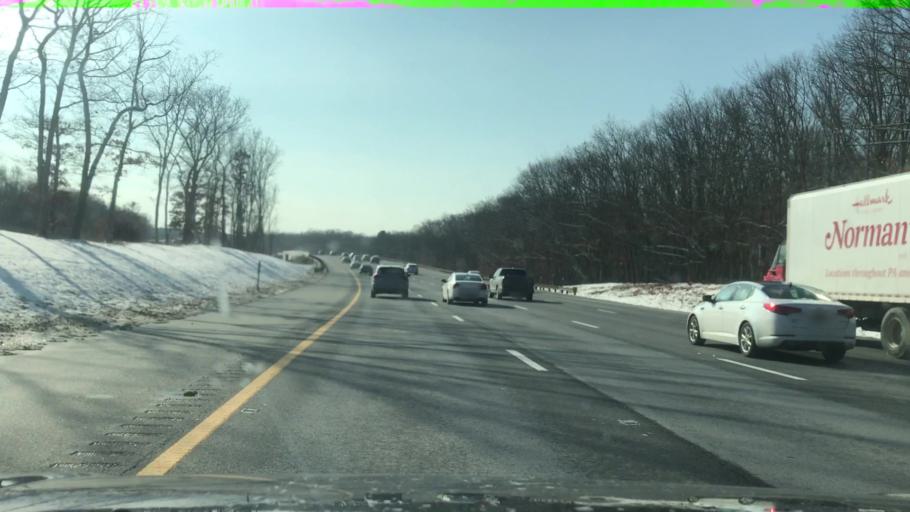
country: US
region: New Jersey
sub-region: Monmouth County
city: Ramtown
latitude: 40.1297
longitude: -74.1239
